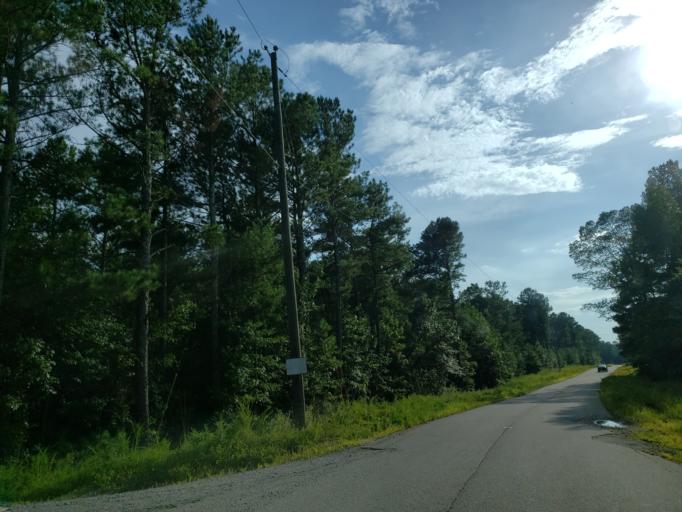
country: US
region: Georgia
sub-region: Bartow County
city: Emerson
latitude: 34.1913
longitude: -84.6489
